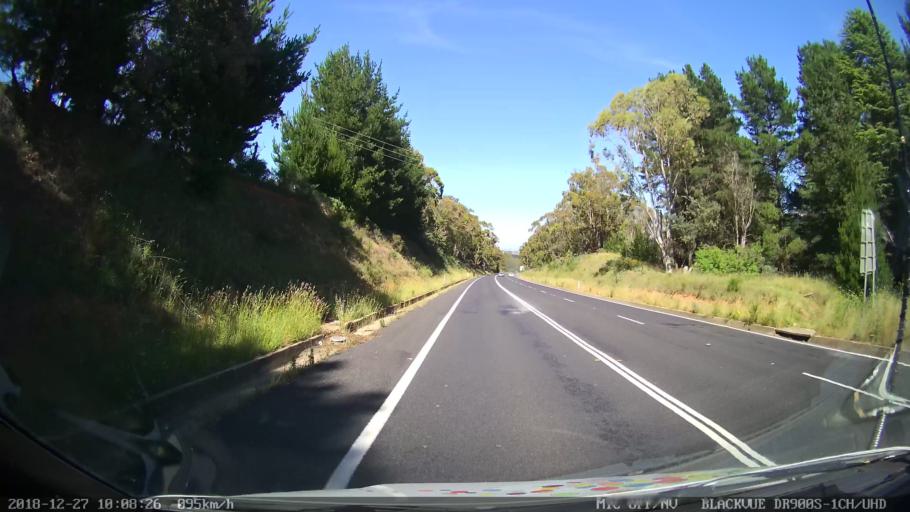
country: AU
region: New South Wales
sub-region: Lithgow
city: Portland
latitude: -33.4477
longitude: 149.8259
